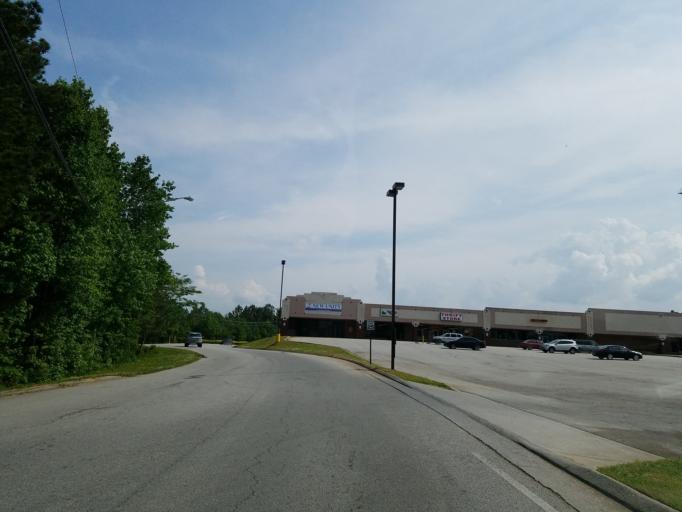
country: US
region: Georgia
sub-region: Paulding County
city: Dallas
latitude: 33.9099
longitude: -84.8034
